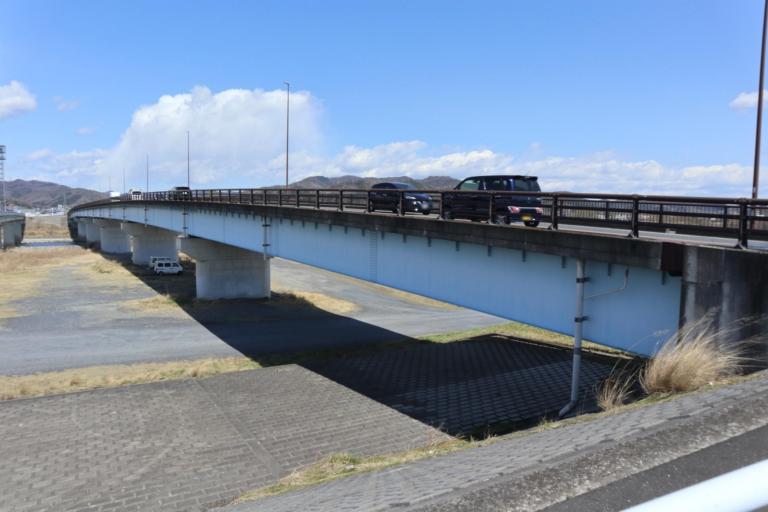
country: JP
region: Gunma
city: Ota
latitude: 36.3554
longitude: 139.3851
